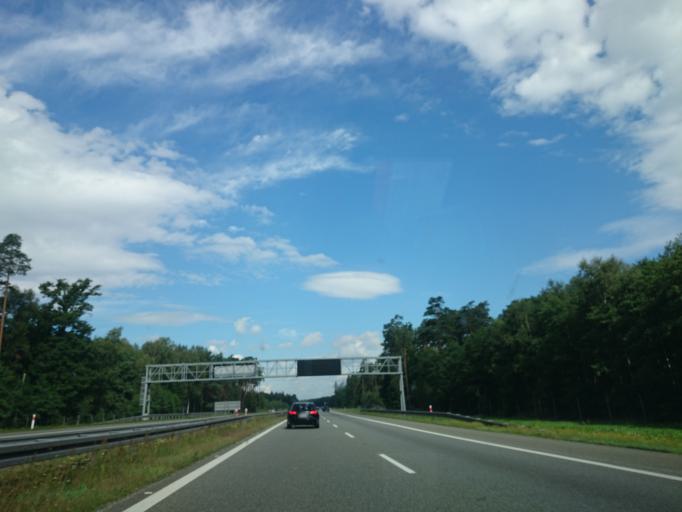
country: PL
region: Opole Voivodeship
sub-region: Powiat opolski
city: Proszkow
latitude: 50.5384
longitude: 17.9023
